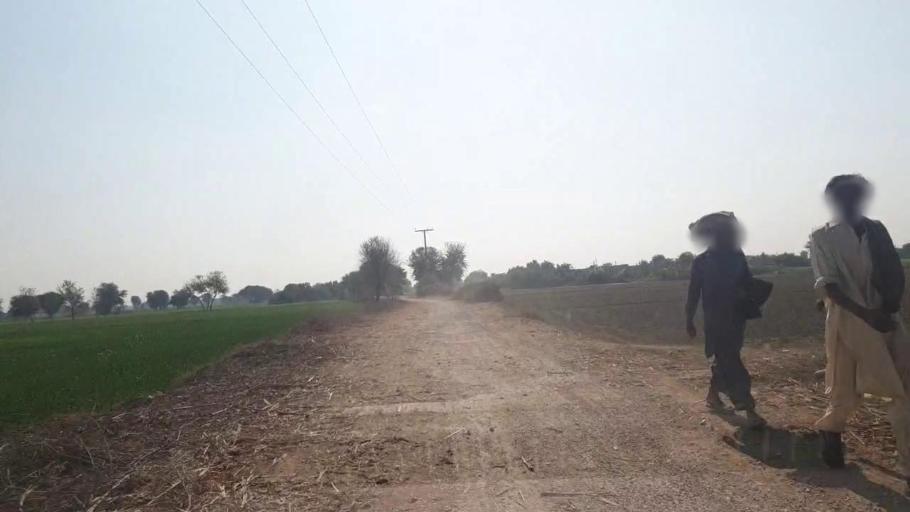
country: PK
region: Sindh
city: Shahdadpur
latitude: 26.0427
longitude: 68.4626
